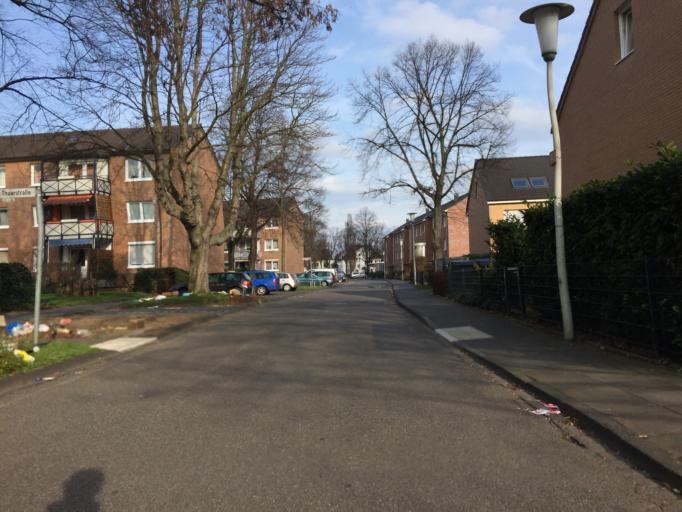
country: DE
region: North Rhine-Westphalia
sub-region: Regierungsbezirk Koln
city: Bonn
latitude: 50.7472
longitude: 7.0793
